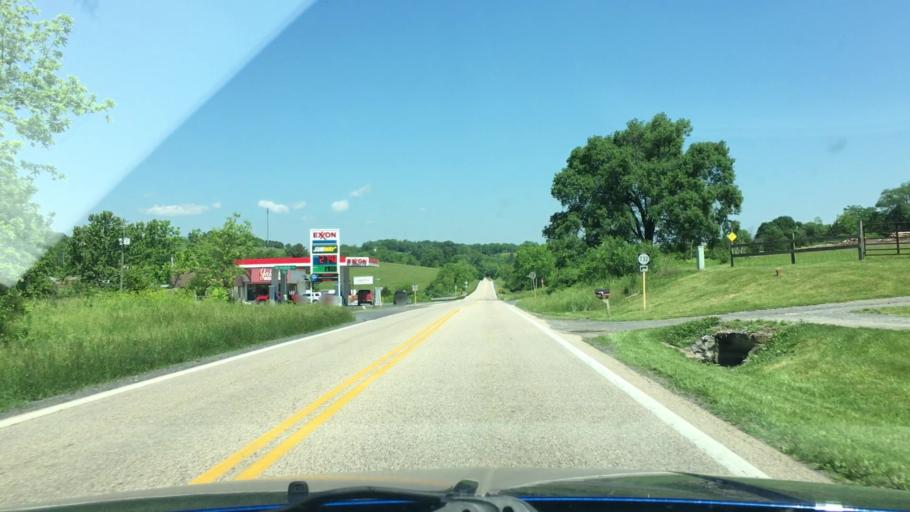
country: US
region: Virginia
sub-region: City of Staunton
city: Staunton
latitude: 38.1976
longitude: -79.1153
